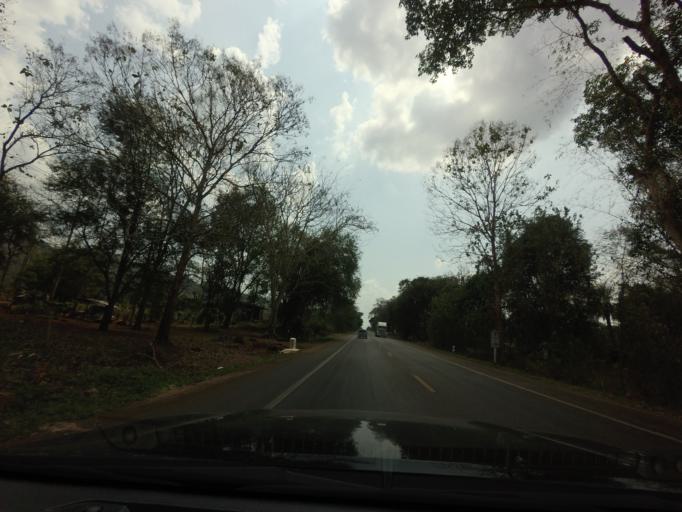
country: TH
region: Kanchanaburi
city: Sai Yok
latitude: 14.1583
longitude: 99.1384
